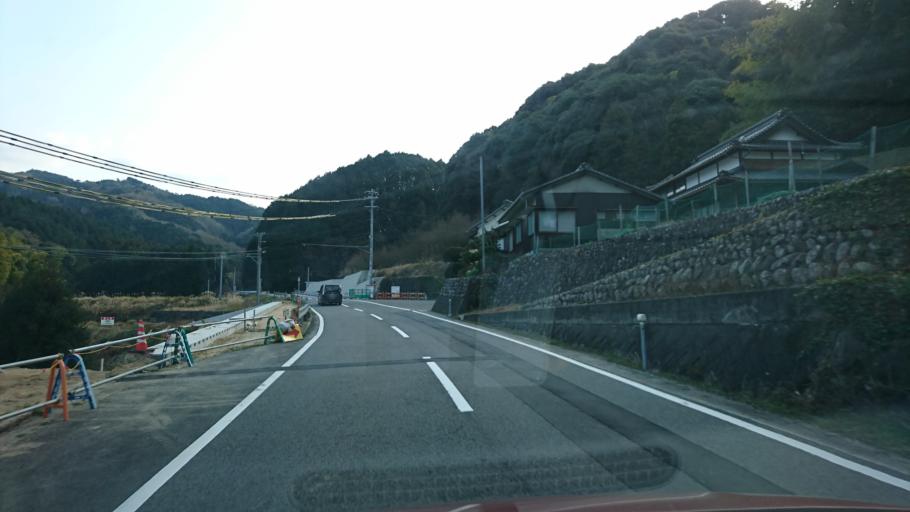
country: JP
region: Ehime
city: Hojo
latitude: 33.9862
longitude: 132.9080
